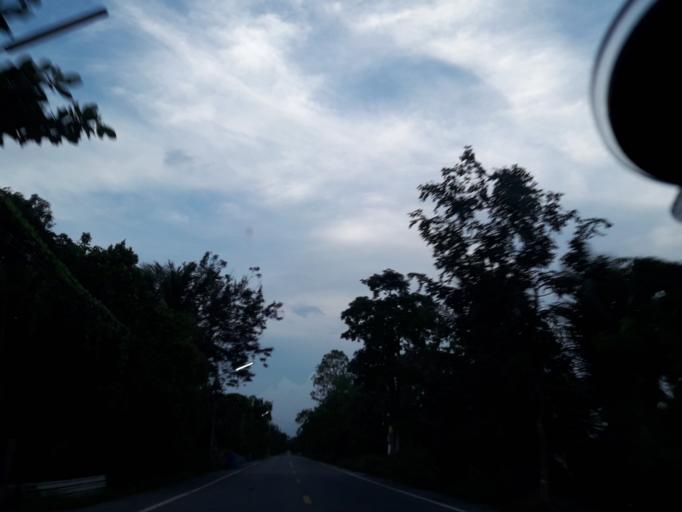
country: TH
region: Pathum Thani
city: Nong Suea
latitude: 14.1585
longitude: 100.8690
